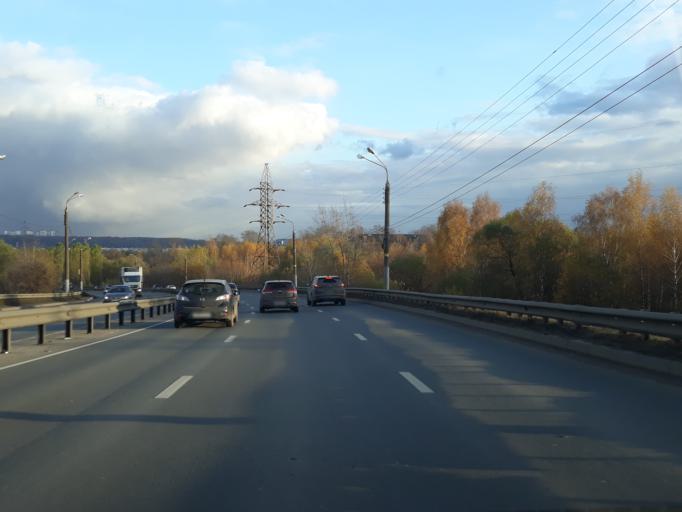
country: RU
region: Nizjnij Novgorod
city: Nizhniy Novgorod
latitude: 56.3053
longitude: 43.9071
